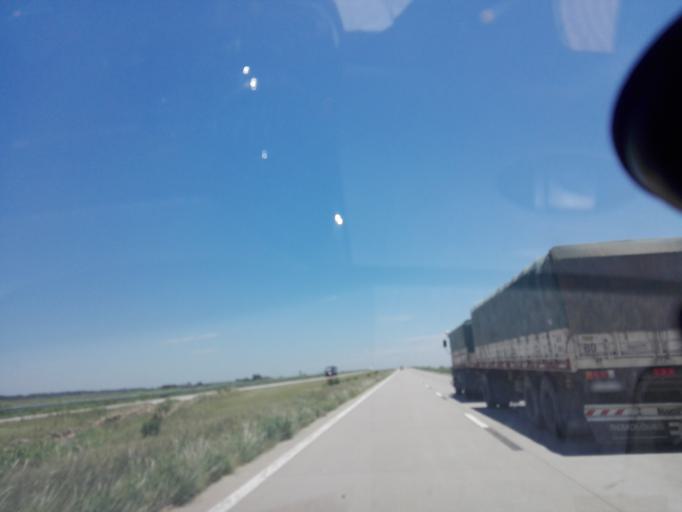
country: AR
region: Cordoba
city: Morrison
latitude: -32.5269
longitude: -62.9362
